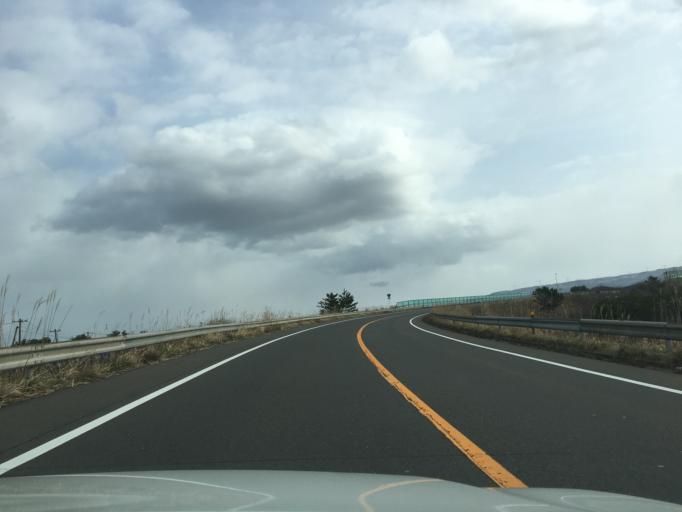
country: JP
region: Yamagata
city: Yuza
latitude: 39.2416
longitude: 139.9140
